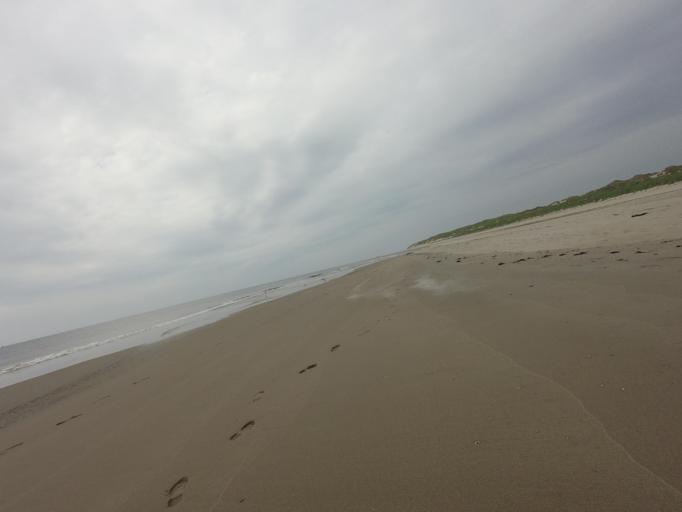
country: NL
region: North Holland
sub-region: Gemeente Den Helder
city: Den Helder
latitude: 53.0046
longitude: 4.7113
